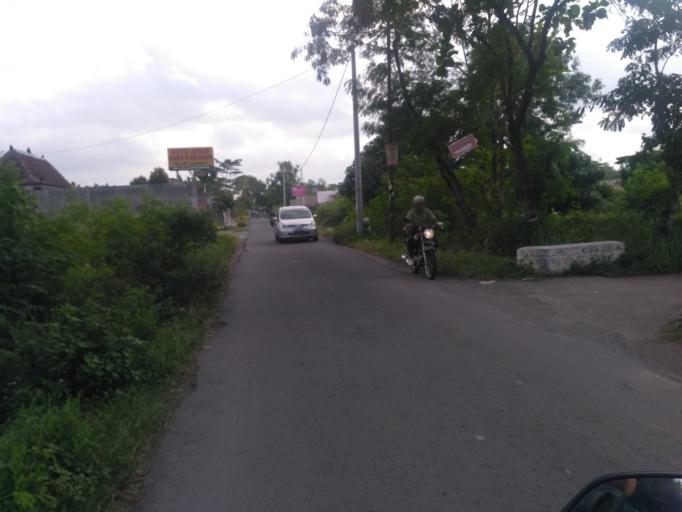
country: ID
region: Daerah Istimewa Yogyakarta
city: Yogyakarta
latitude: -7.7701
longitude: 110.3588
